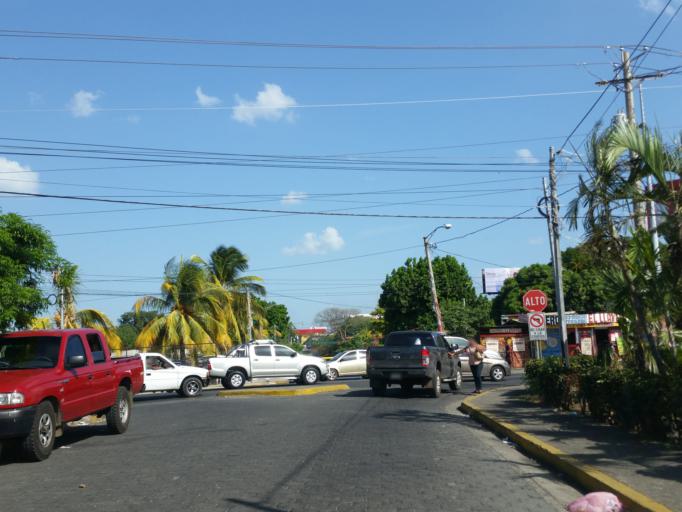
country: NI
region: Managua
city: Managua
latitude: 12.1144
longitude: -86.2548
